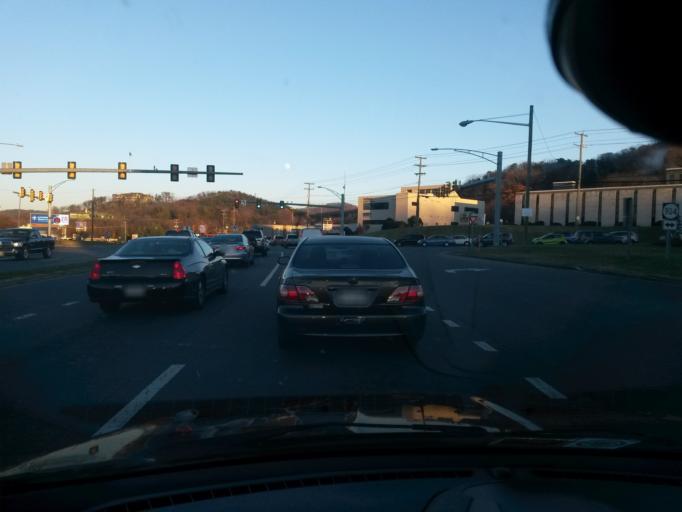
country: US
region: Virginia
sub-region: Roanoke County
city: Cave Spring
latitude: 37.2237
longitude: -79.9853
